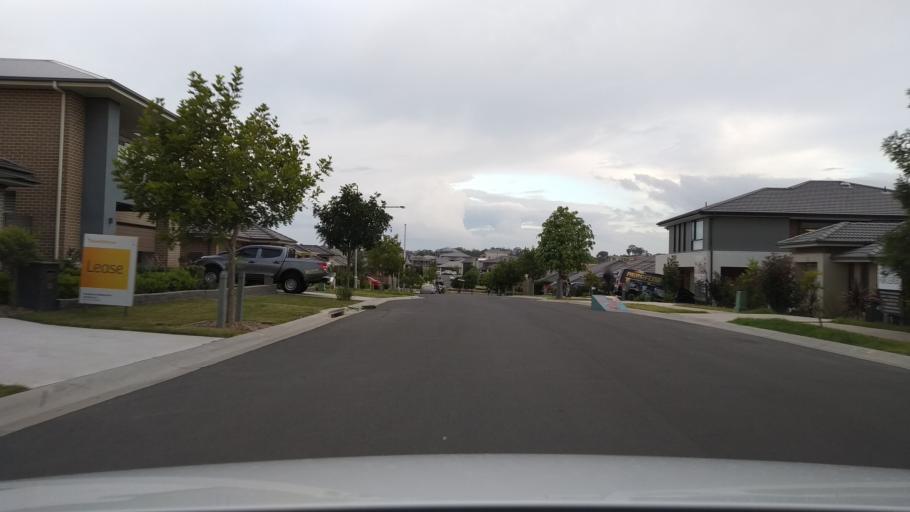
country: AU
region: New South Wales
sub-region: Camden
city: Narellan
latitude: -34.0039
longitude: 150.7279
